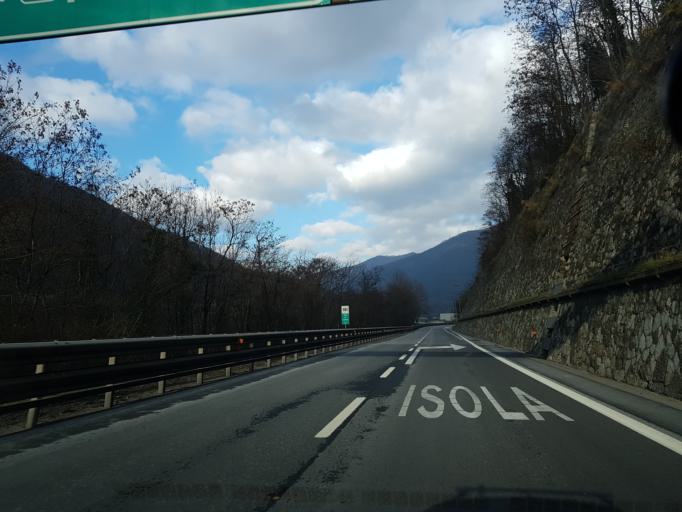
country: IT
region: Liguria
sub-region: Provincia di Genova
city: Isola del Cantone
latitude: 44.6376
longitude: 8.9531
